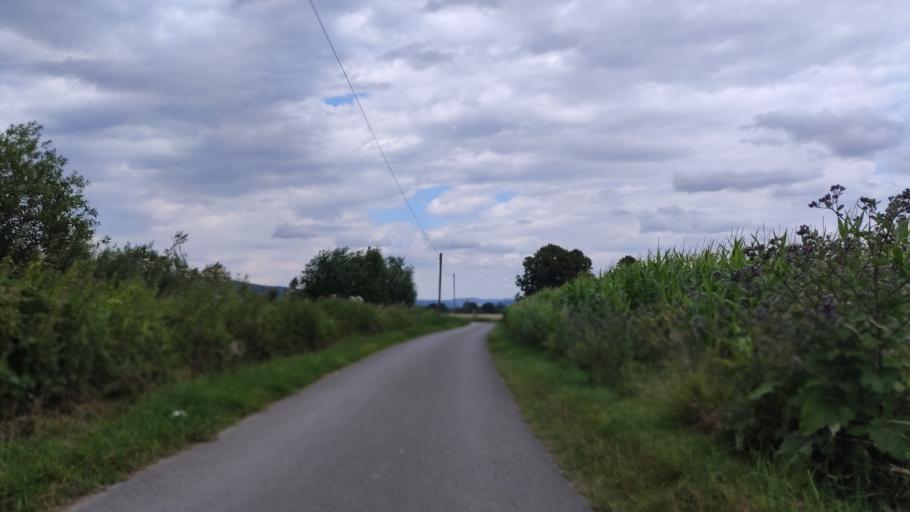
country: DE
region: Lower Saxony
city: Holzminden
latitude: 51.8127
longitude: 9.4263
